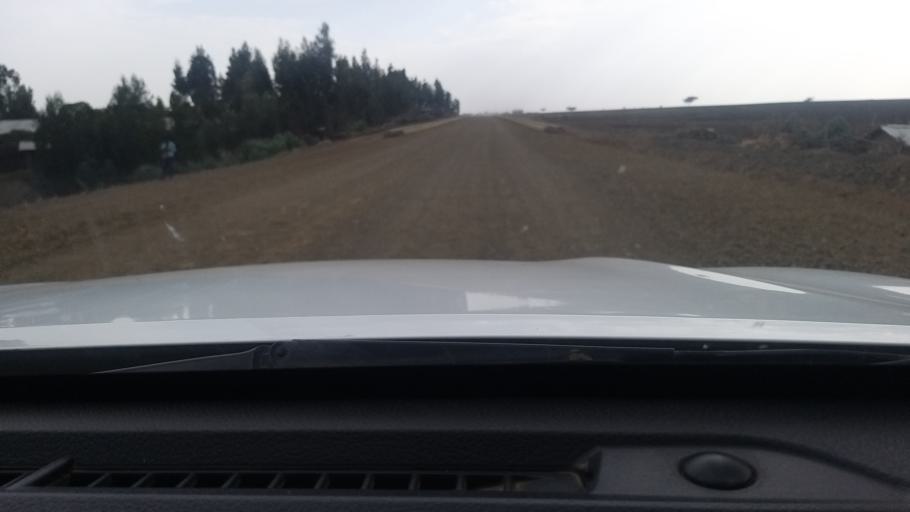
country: ET
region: Amhara
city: Were Ilu
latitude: 10.4491
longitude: 39.2032
